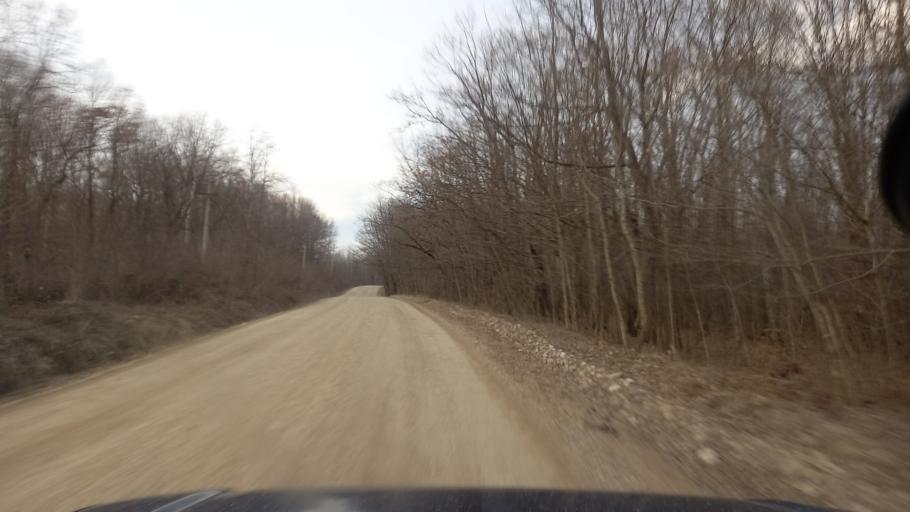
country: RU
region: Adygeya
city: Kamennomostskiy
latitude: 44.1503
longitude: 40.2477
